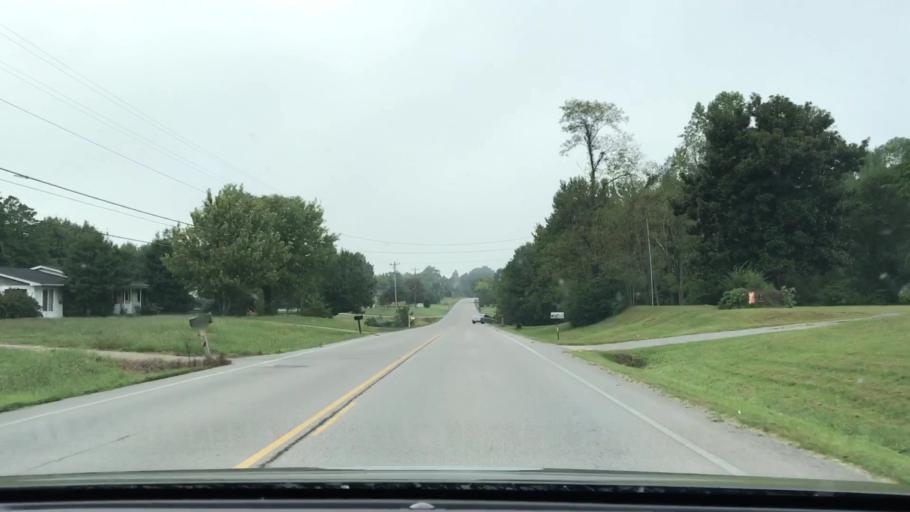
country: US
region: Tennessee
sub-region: Sumner County
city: Portland
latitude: 36.4934
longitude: -86.4951
